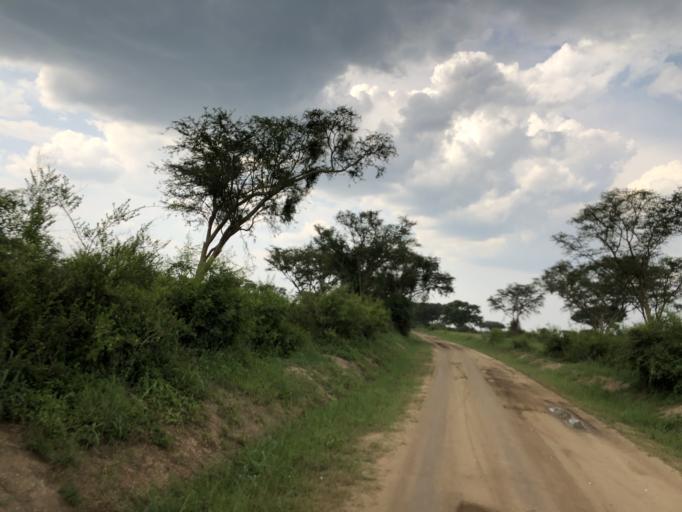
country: UG
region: Western Region
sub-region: Rubirizi District
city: Rubirizi
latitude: -0.1992
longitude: 30.0036
